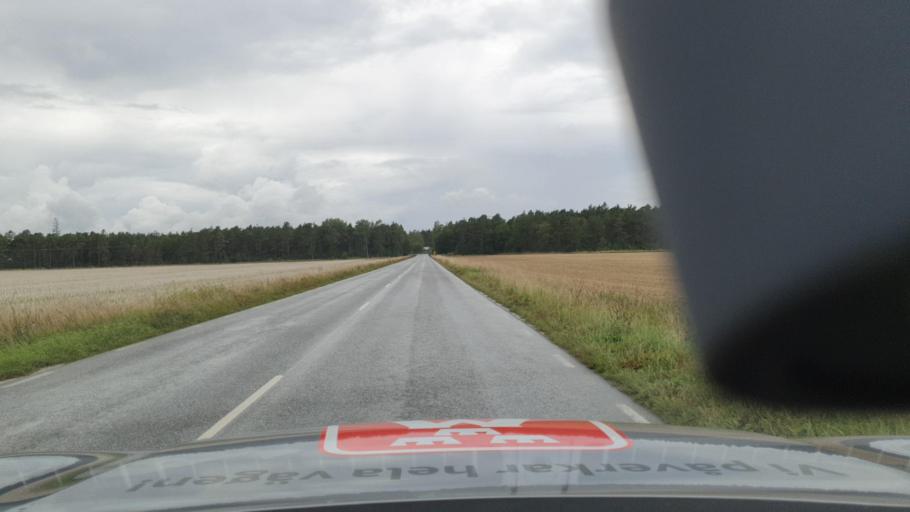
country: SE
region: Gotland
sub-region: Gotland
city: Vibble
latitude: 57.4974
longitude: 18.3770
